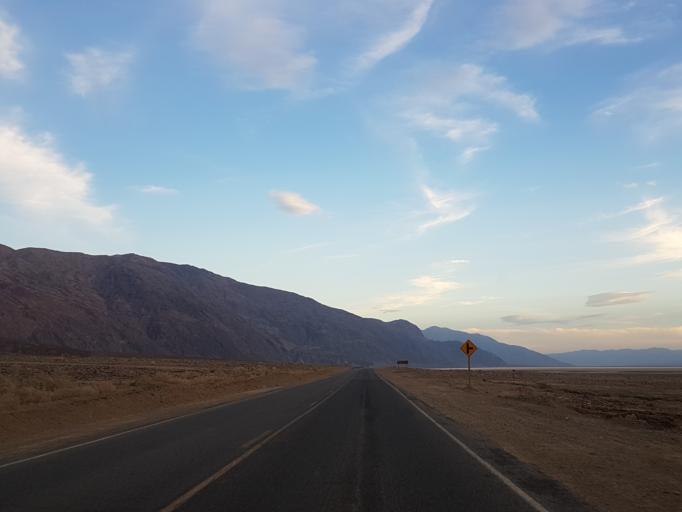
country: US
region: Nevada
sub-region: Nye County
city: Beatty
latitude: 36.3006
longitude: -116.8129
